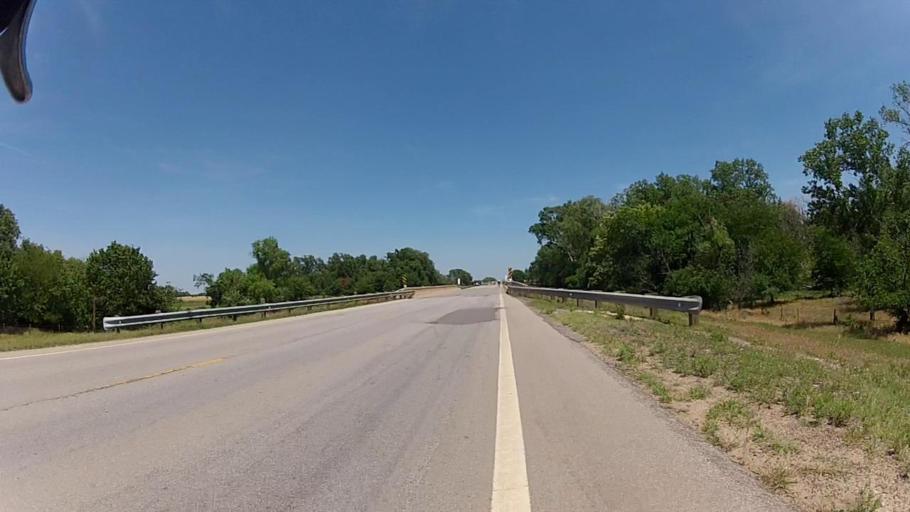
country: US
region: Kansas
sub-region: Harper County
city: Harper
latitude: 37.2388
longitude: -98.0958
